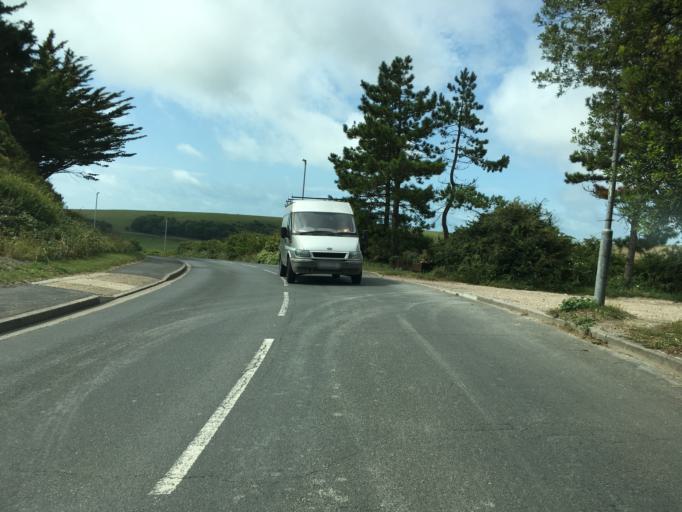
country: GB
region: England
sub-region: Brighton and Hove
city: Rottingdean
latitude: 50.8206
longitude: -0.0731
